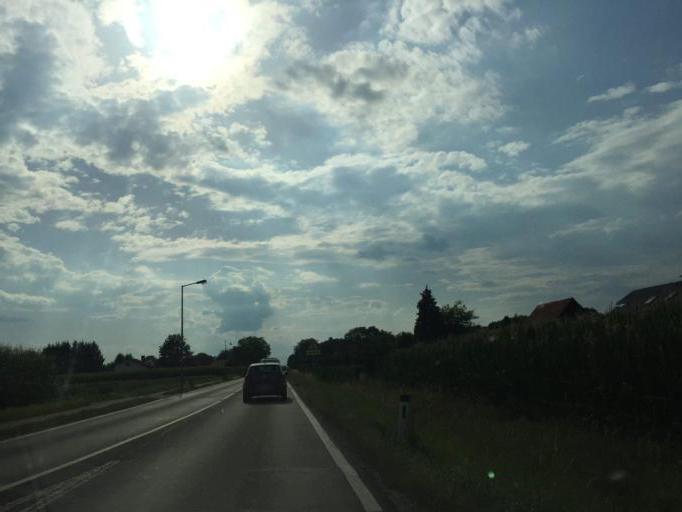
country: AT
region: Styria
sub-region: Politischer Bezirk Suedoststeiermark
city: Eichfeld
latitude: 46.7261
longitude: 15.7598
